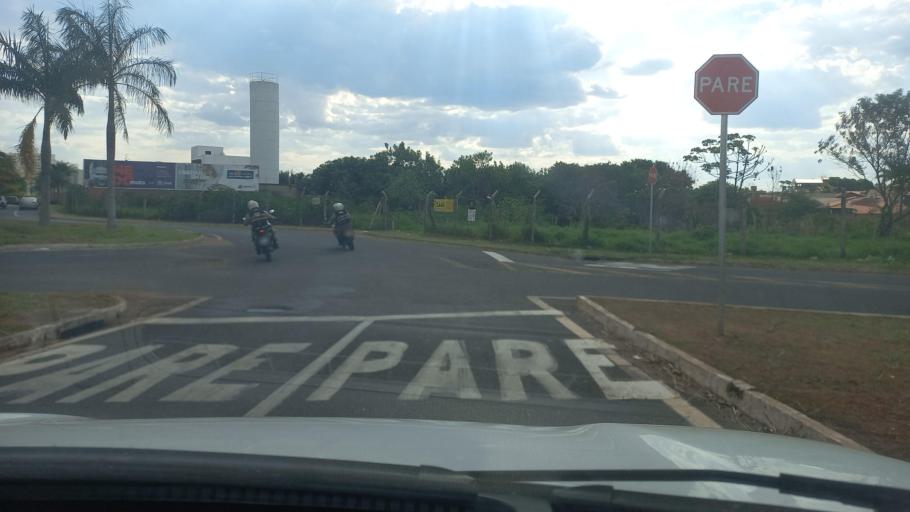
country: BR
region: Minas Gerais
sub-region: Uberaba
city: Uberaba
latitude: -19.7433
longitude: -47.9050
